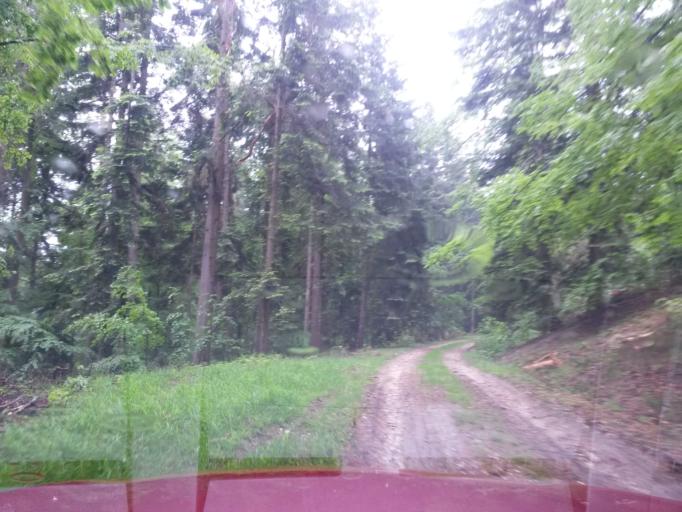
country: SK
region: Kosicky
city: Medzev
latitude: 48.7803
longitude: 20.7846
